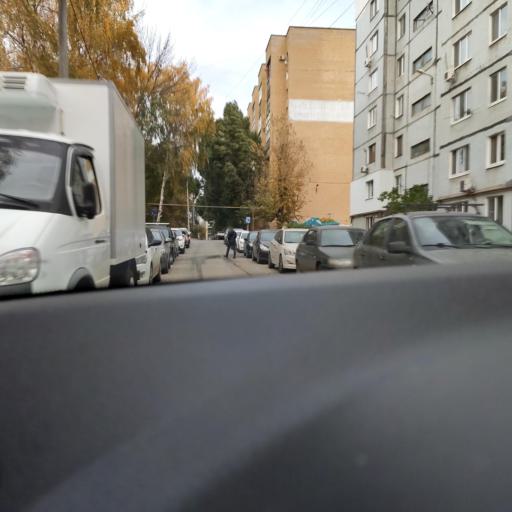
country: RU
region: Samara
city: Samara
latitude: 53.2375
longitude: 50.2512
